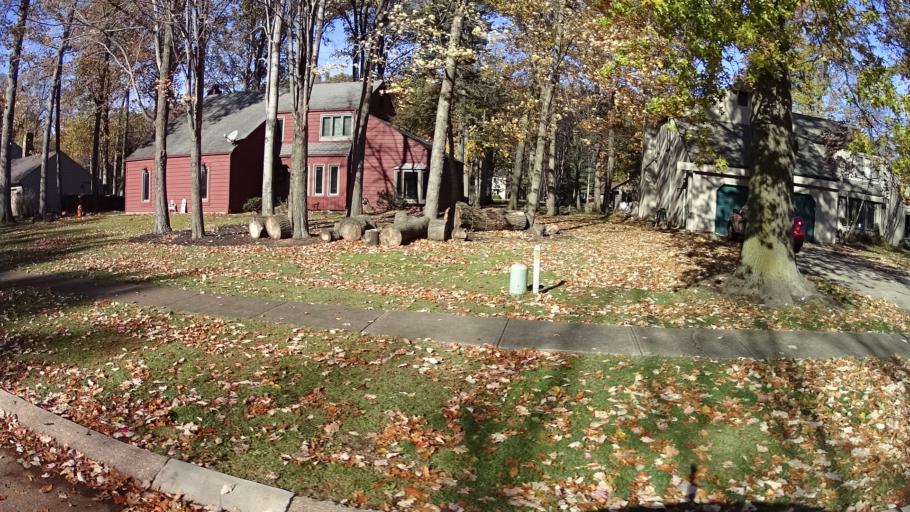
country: US
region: Ohio
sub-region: Lorain County
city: Avon Lake
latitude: 41.4953
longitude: -82.0100
